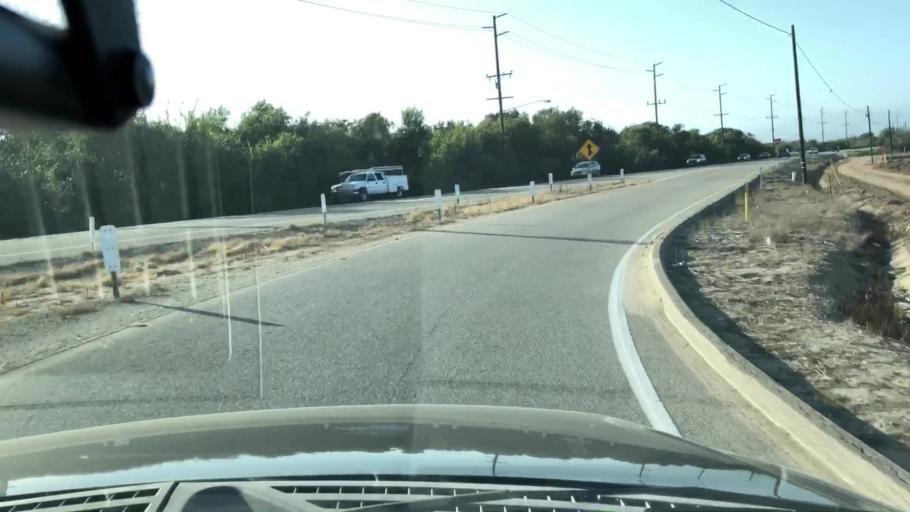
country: US
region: California
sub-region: Ventura County
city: Oxnard Shores
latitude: 34.2189
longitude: -119.2536
